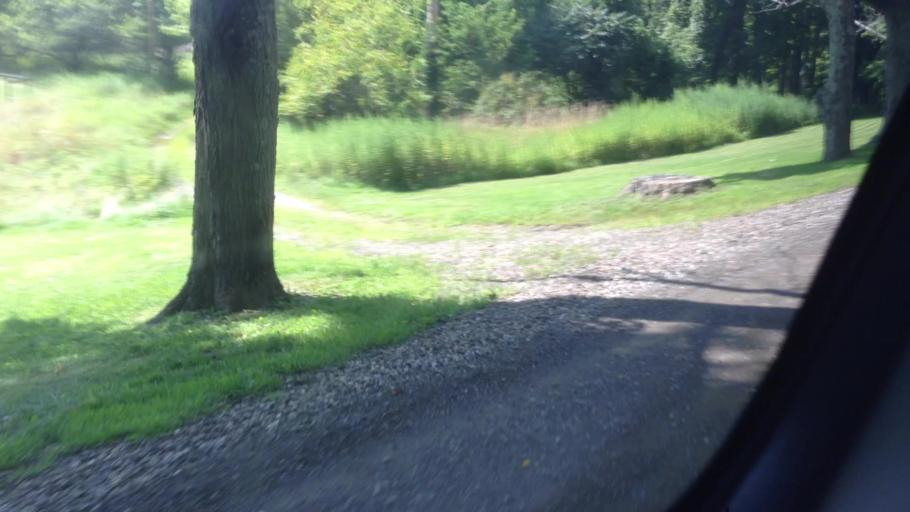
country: US
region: New York
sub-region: Dutchess County
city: Red Hook
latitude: 42.0102
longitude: -73.9116
